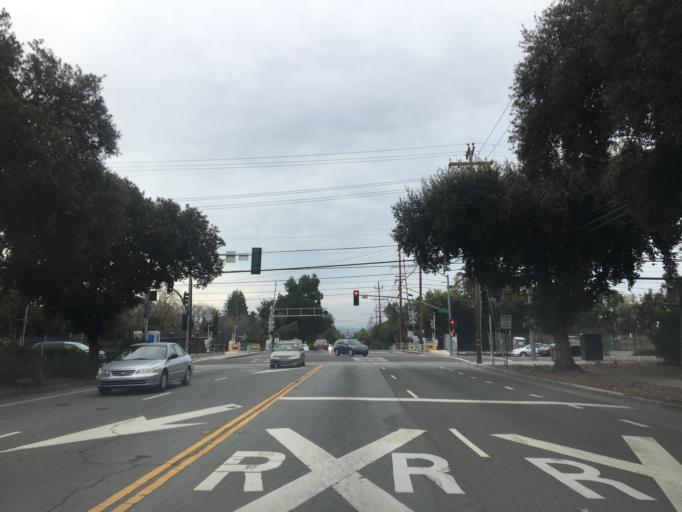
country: US
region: California
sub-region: Santa Clara County
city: Los Altos
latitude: 37.4152
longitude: -122.1180
